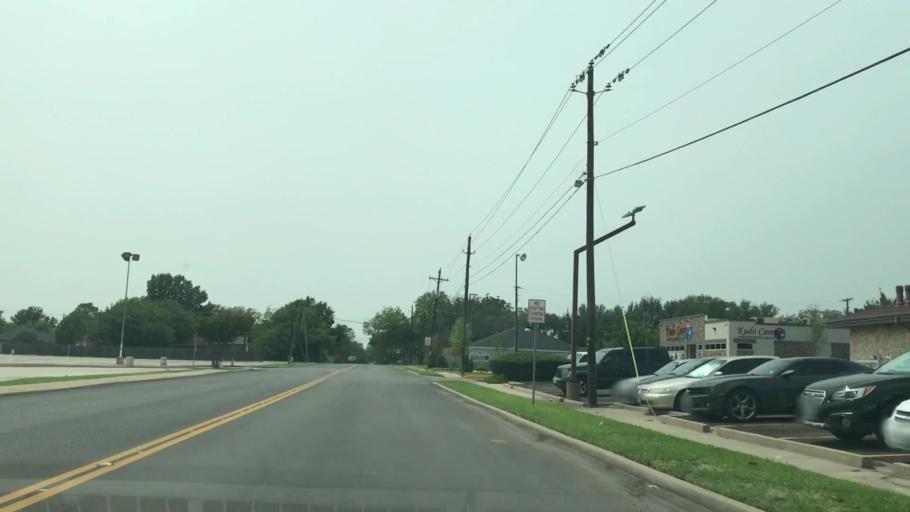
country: US
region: Texas
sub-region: Dallas County
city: Irving
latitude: 32.8434
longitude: -96.9935
